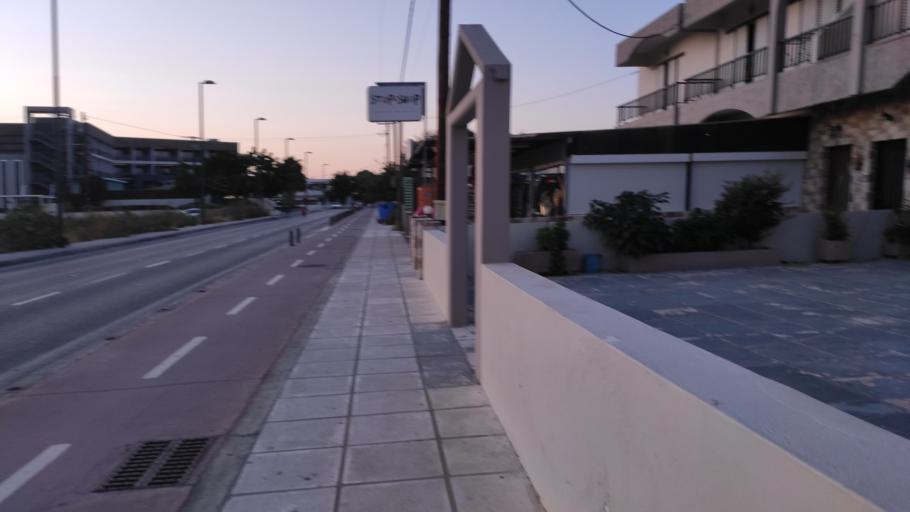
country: GR
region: South Aegean
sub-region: Nomos Dodekanisou
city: Kos
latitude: 36.9132
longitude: 27.2782
